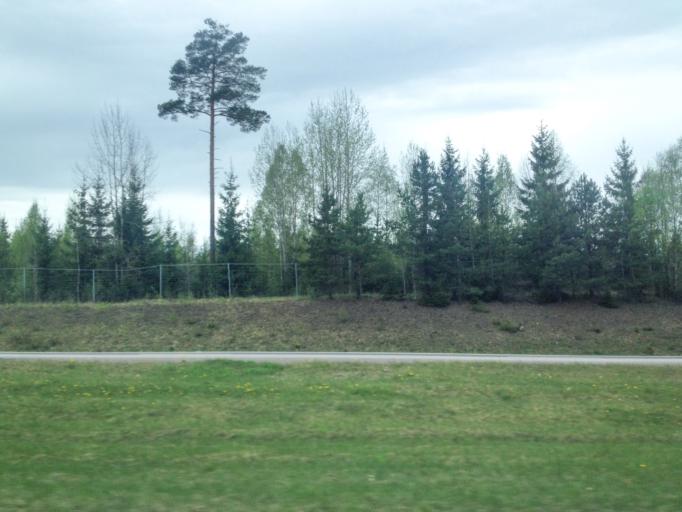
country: FI
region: Uusimaa
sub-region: Helsinki
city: Nurmijaervi
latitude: 60.4701
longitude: 24.8500
